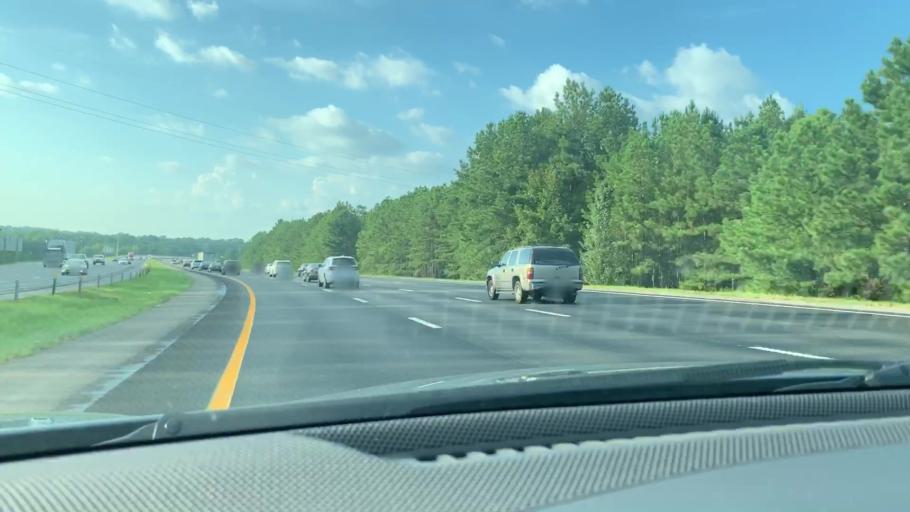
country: US
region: South Carolina
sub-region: Richland County
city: Forest Acres
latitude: 33.9909
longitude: -80.9539
